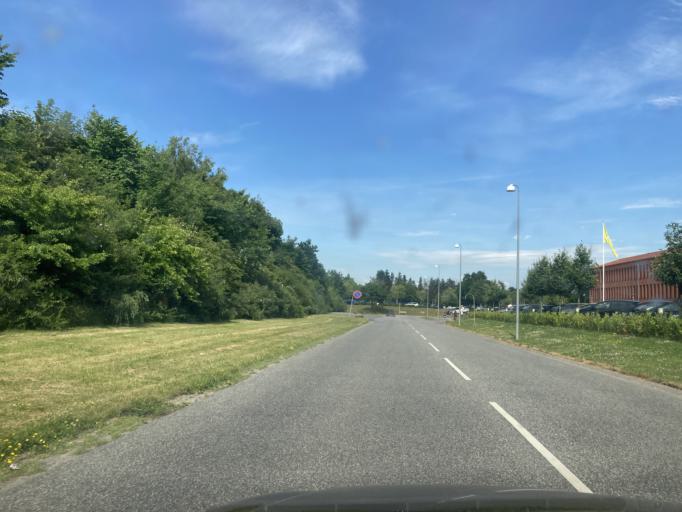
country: DK
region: Capital Region
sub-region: Hillerod Kommune
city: Nodebo
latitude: 55.9350
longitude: 12.3561
